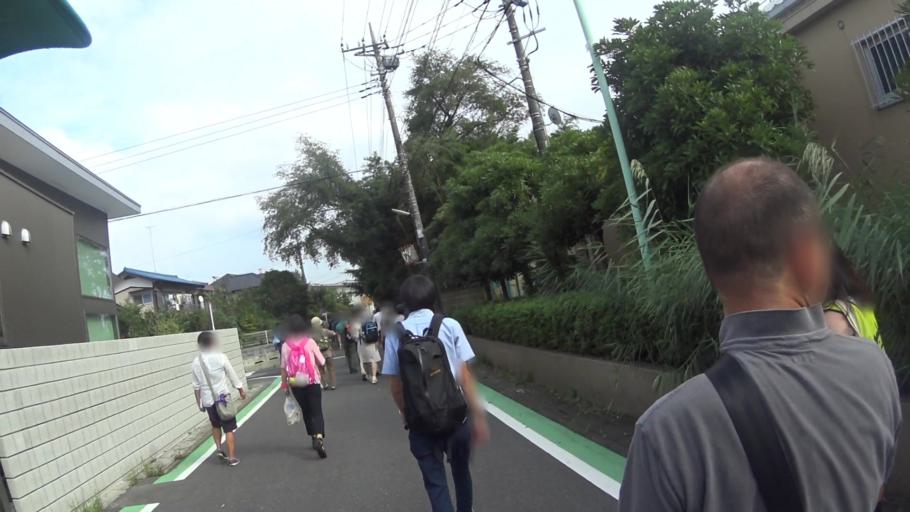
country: JP
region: Saitama
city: Iwatsuki
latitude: 35.9658
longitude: 139.7097
